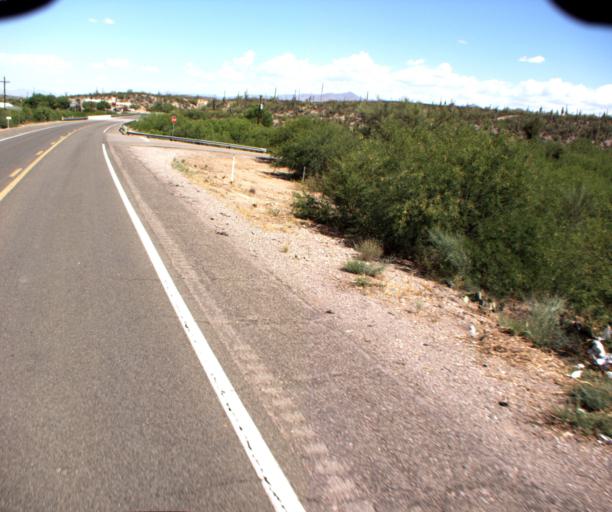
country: US
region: Arizona
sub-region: Pinal County
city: Kearny
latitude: 32.9302
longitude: -110.7327
